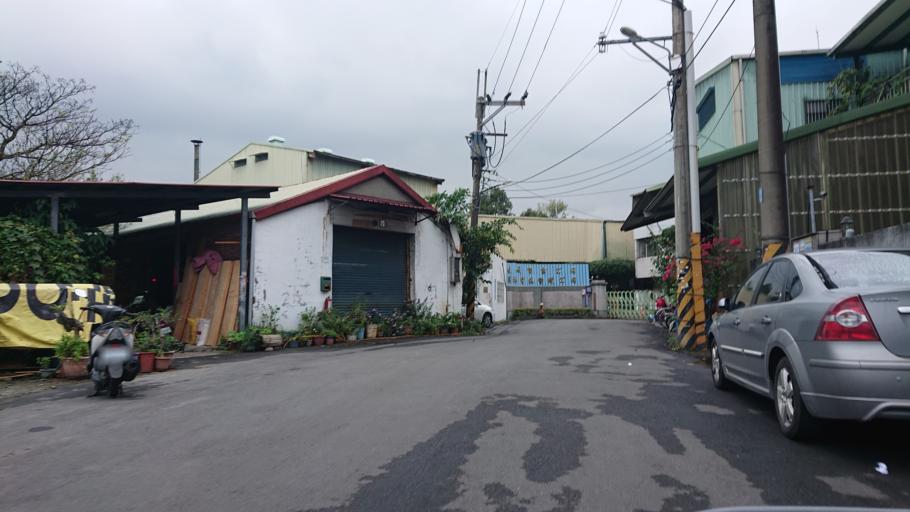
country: TW
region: Taiwan
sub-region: Taoyuan
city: Taoyuan
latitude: 24.9445
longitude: 121.3900
